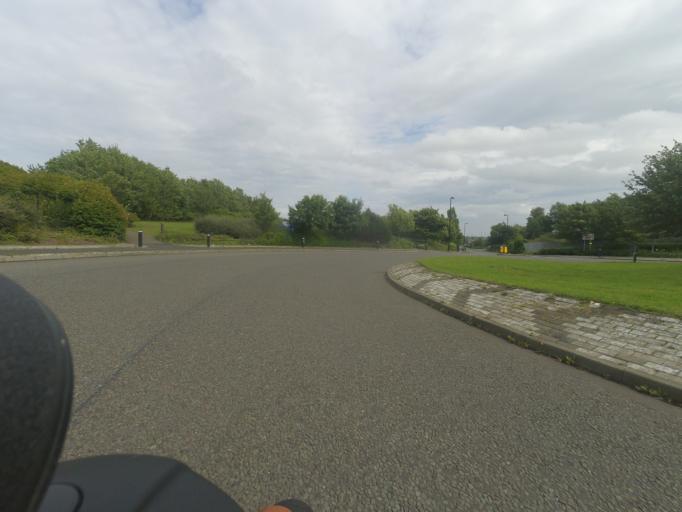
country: GB
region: England
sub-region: Borough of North Tyneside
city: North Shields
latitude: 54.9953
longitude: -1.4605
